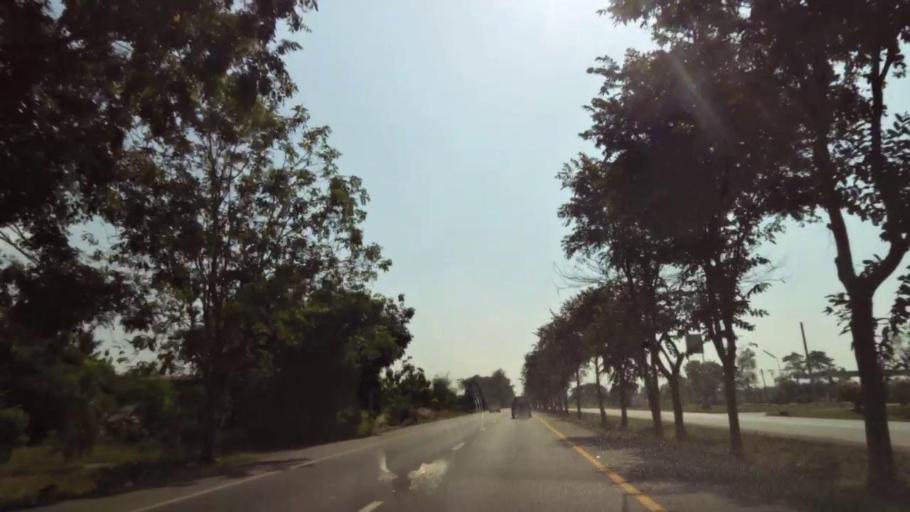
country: TH
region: Phichit
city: Bueng Na Rang
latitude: 16.0939
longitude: 100.1253
